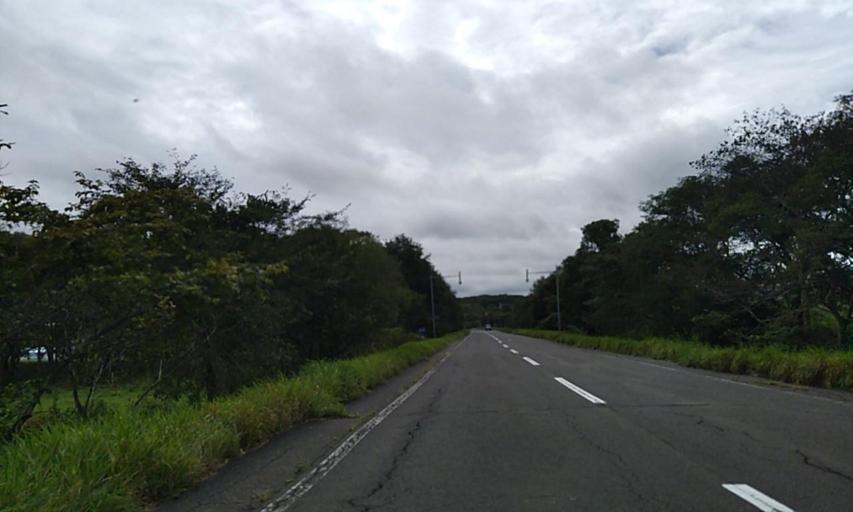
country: JP
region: Hokkaido
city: Shibetsu
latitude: 43.3317
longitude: 145.2151
